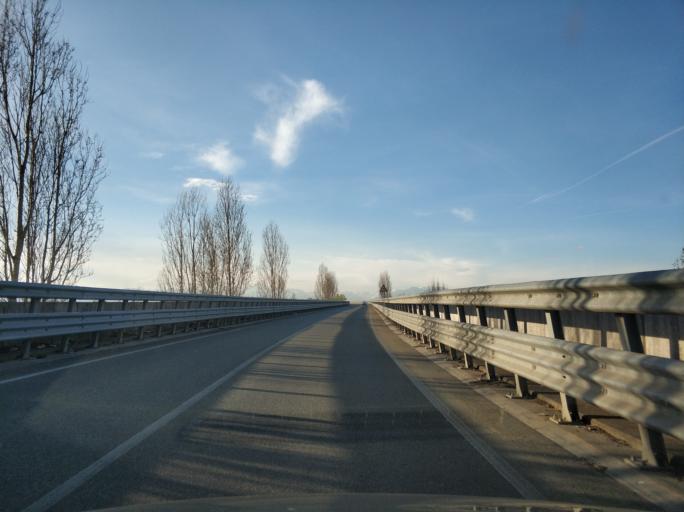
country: IT
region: Piedmont
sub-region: Provincia di Torino
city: Brandizzo
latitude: 45.1842
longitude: 7.8425
